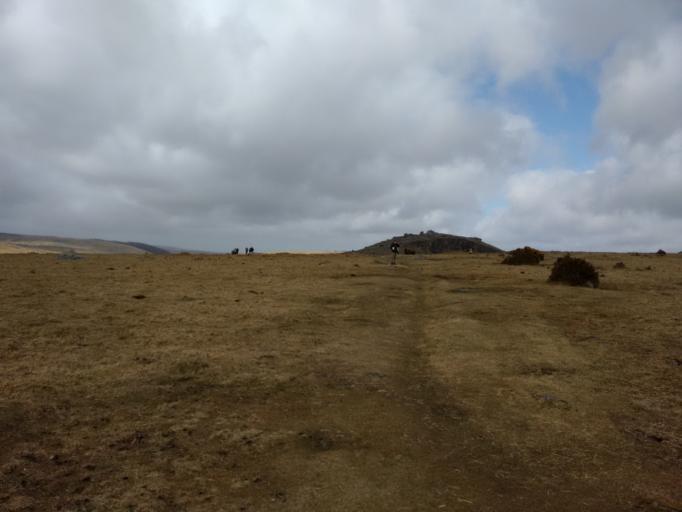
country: GB
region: England
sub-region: Cornwall
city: North Hill
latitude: 50.5203
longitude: -4.4581
